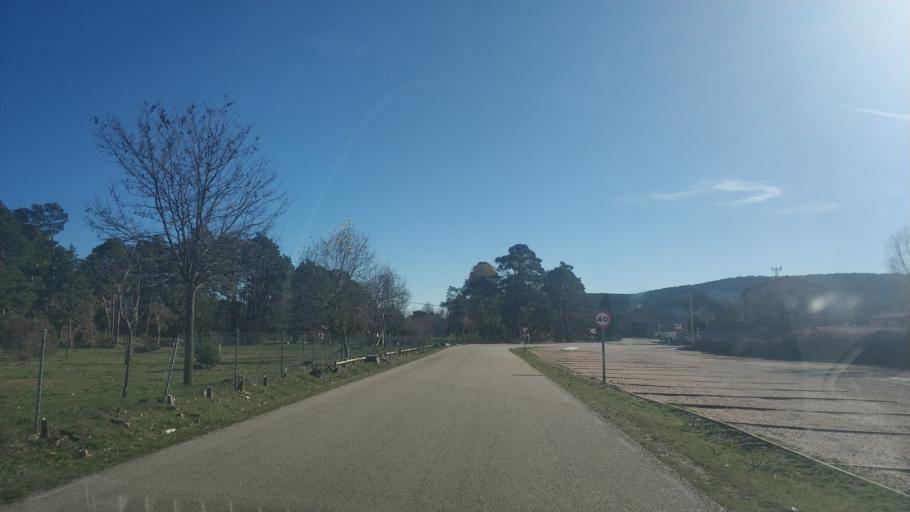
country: ES
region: Castille and Leon
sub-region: Provincia de Soria
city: Vinuesa
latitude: 41.9129
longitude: -2.7599
